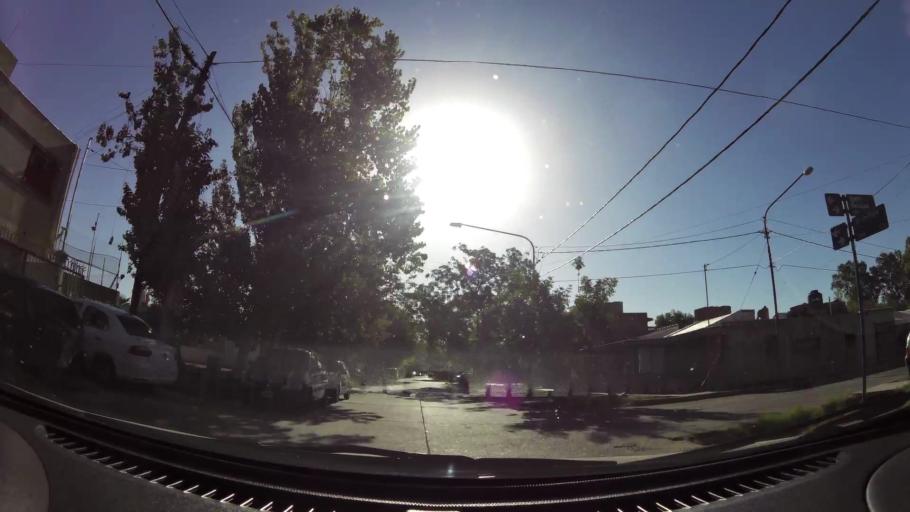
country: AR
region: Mendoza
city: Mendoza
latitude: -32.9005
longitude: -68.8079
